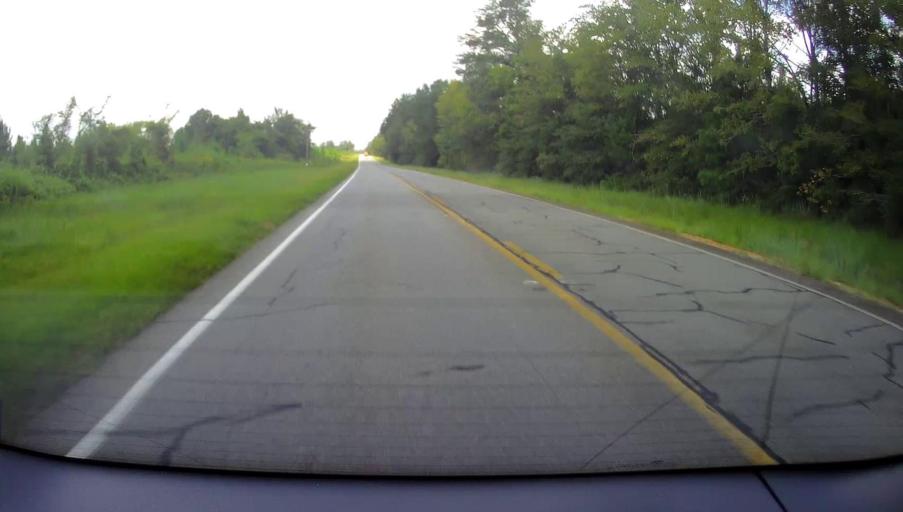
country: US
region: Georgia
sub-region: Houston County
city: Robins Air Force Base
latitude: 32.6348
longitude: -83.4986
